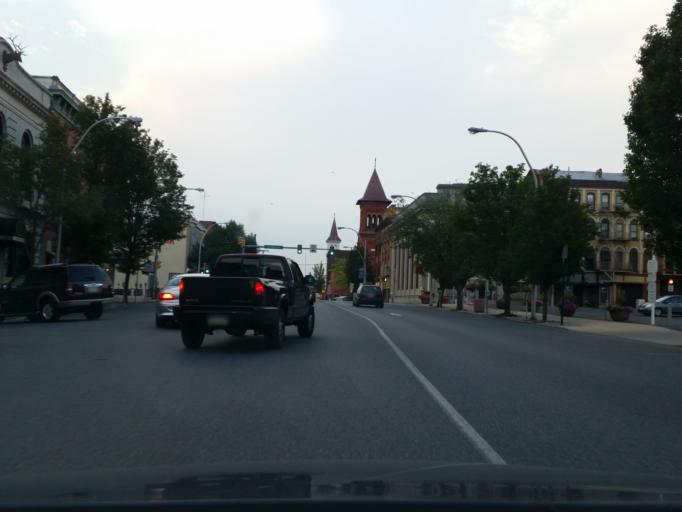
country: US
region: Pennsylvania
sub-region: Lebanon County
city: Lebanon
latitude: 40.3385
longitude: -76.4262
